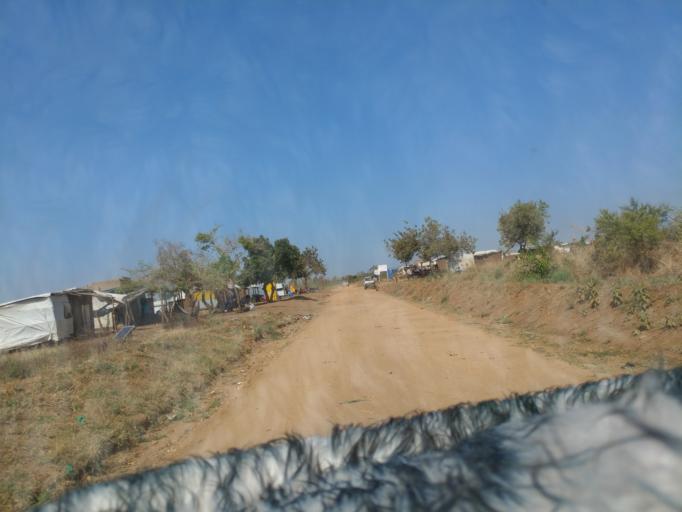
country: UG
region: Northern Region
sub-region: Yumbe District
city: Yumbe
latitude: 3.3916
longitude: 31.3481
